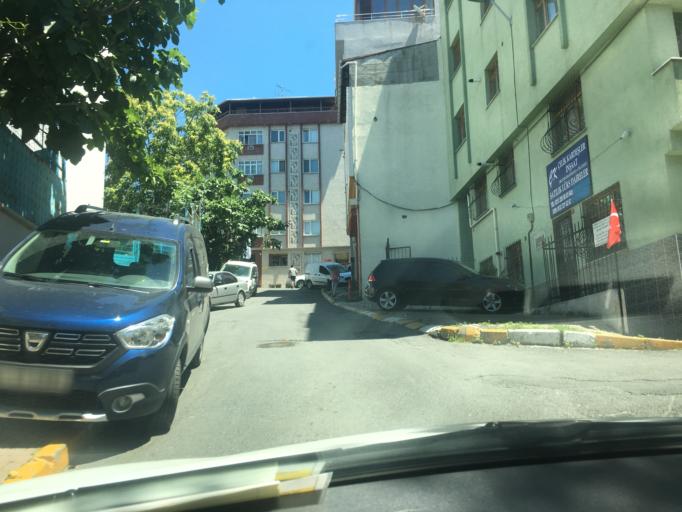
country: TR
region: Istanbul
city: Istanbul
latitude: 41.0496
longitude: 28.9438
